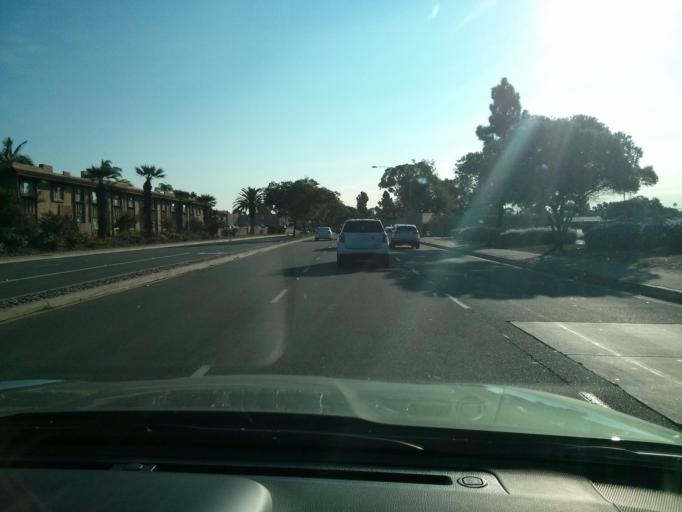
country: US
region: California
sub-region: San Diego County
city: San Diego
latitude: 32.8203
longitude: -117.1714
